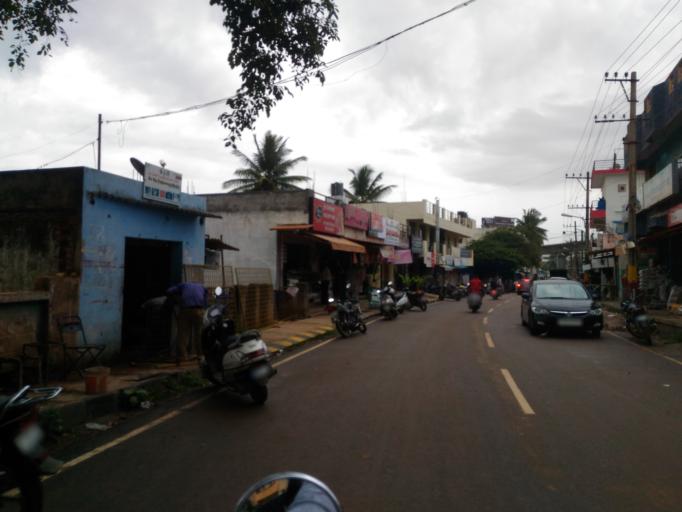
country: IN
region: Karnataka
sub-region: Bangalore Urban
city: Bangalore
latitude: 12.8748
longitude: 77.5401
